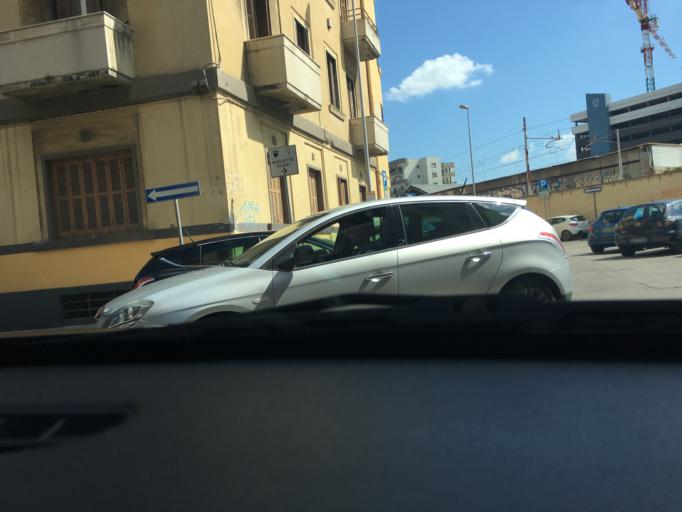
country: IT
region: Apulia
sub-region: Provincia di Bari
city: Bari
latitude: 41.1186
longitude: 16.8808
